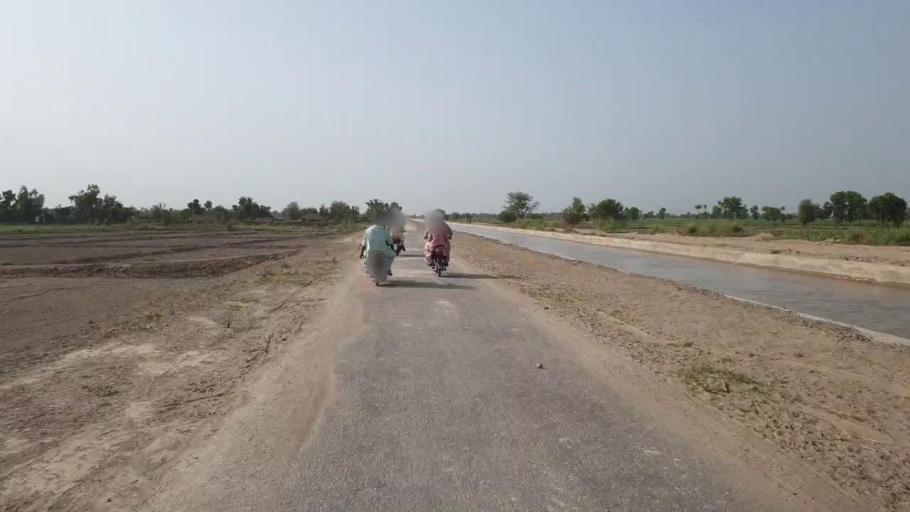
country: PK
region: Sindh
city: Daur
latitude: 26.3383
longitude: 68.1634
